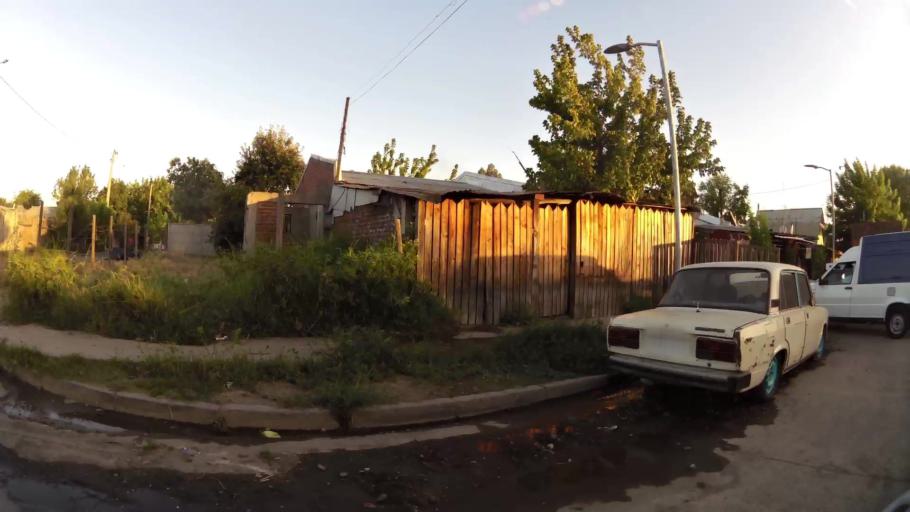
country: CL
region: Maule
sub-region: Provincia de Talca
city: Talca
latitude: -35.4474
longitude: -71.6375
